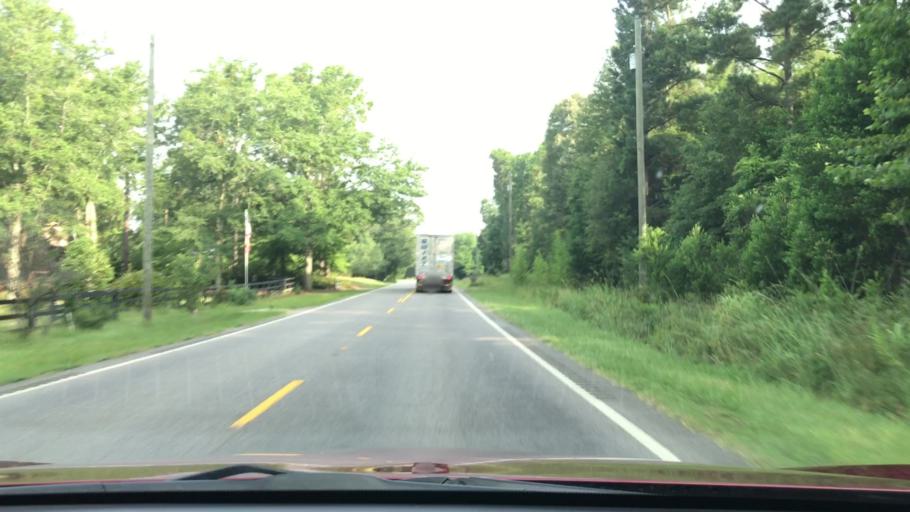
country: US
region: South Carolina
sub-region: Barnwell County
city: Williston
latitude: 33.6179
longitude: -81.2875
